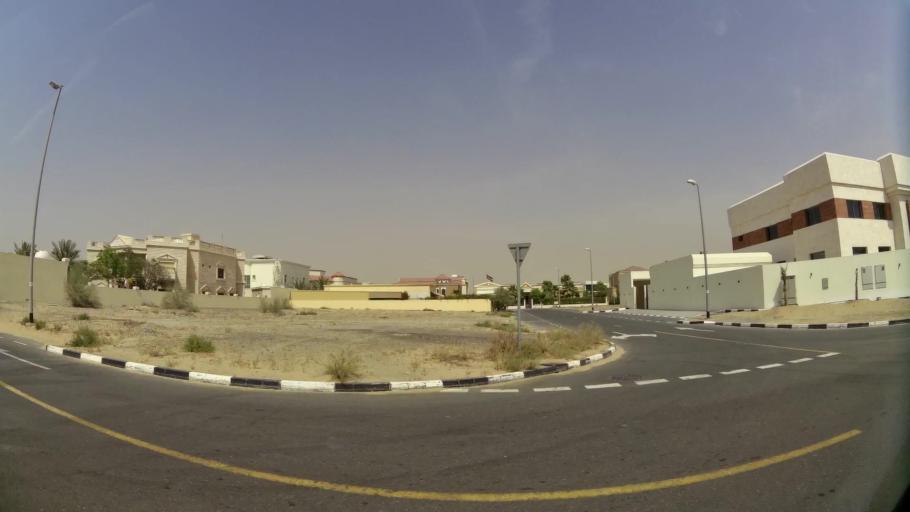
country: AE
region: Ash Shariqah
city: Sharjah
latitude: 25.2494
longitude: 55.4890
